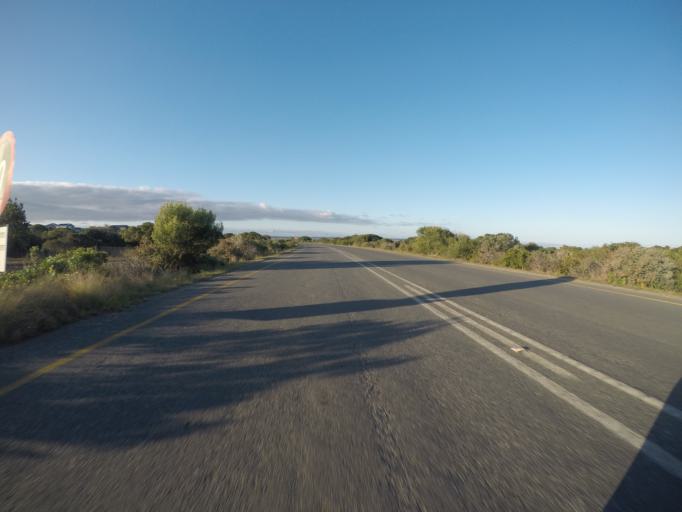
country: ZA
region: Western Cape
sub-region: Eden District Municipality
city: Riversdale
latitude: -34.3861
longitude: 21.4035
